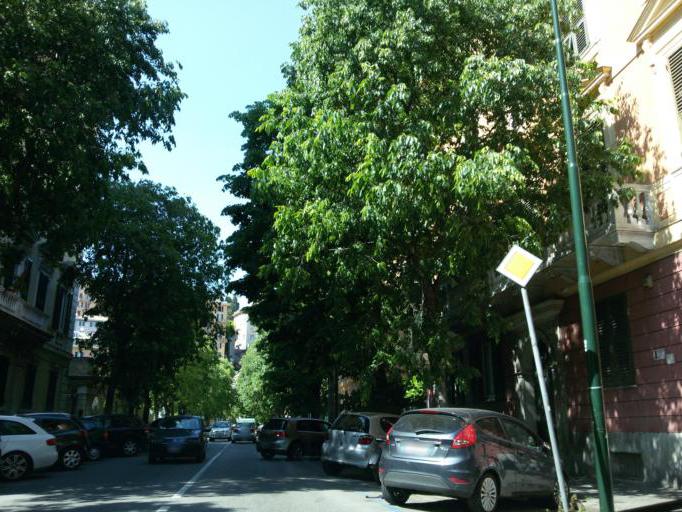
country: IT
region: Liguria
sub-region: Provincia di Genova
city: Genoa
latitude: 44.4148
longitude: 8.9360
